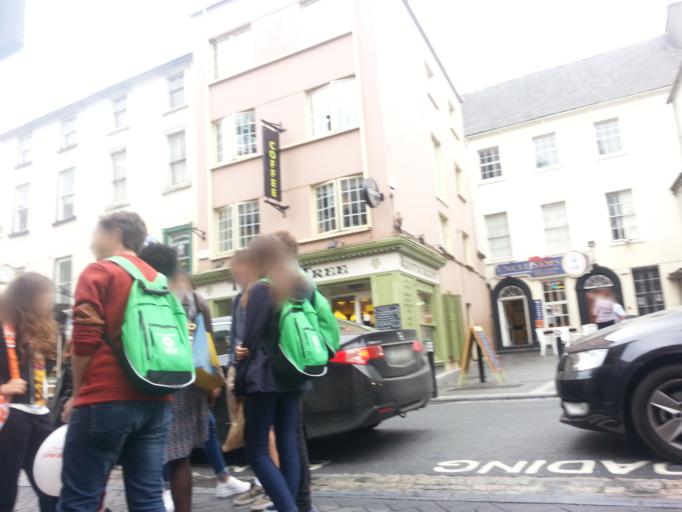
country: IE
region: Leinster
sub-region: Kilkenny
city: Kilkenny
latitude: 52.6517
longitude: -7.2529
